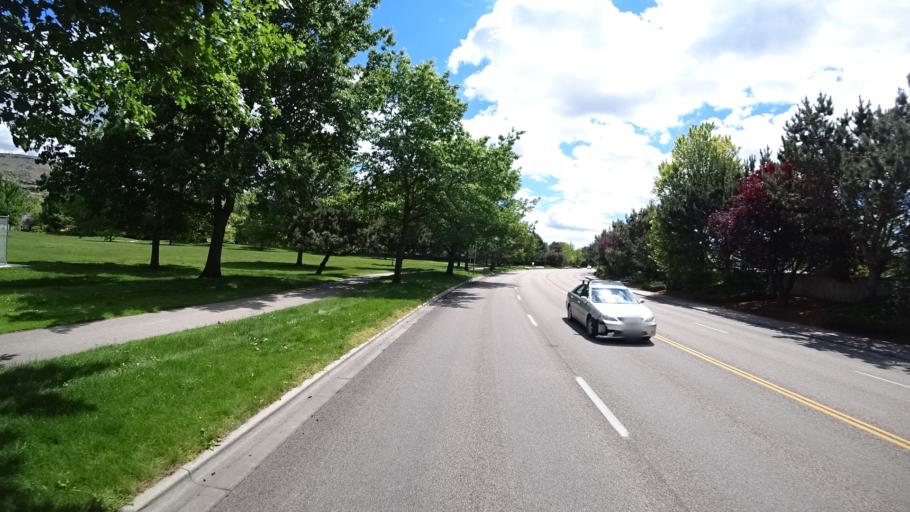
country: US
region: Idaho
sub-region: Ada County
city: Boise
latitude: 43.5821
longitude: -116.1647
